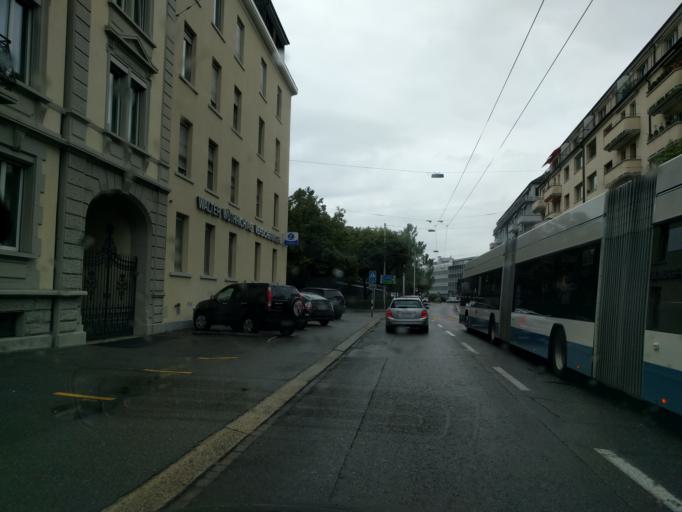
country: CH
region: Zurich
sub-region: Bezirk Zuerich
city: Zurich
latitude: 47.3653
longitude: 8.5541
